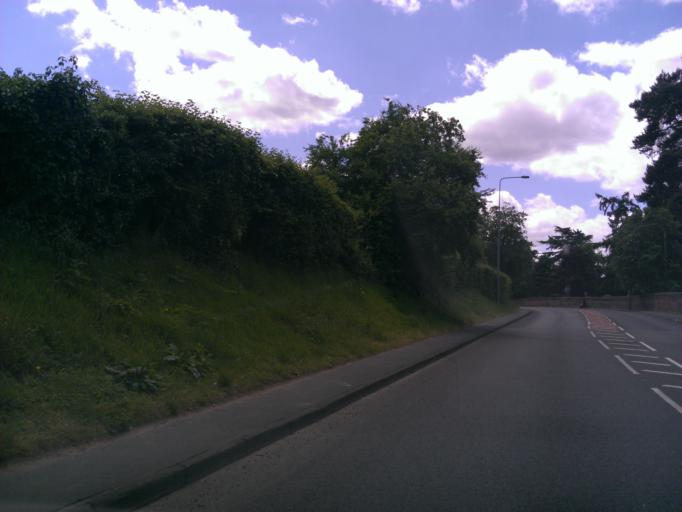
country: GB
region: England
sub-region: Essex
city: Colchester
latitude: 51.8754
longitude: 0.9088
